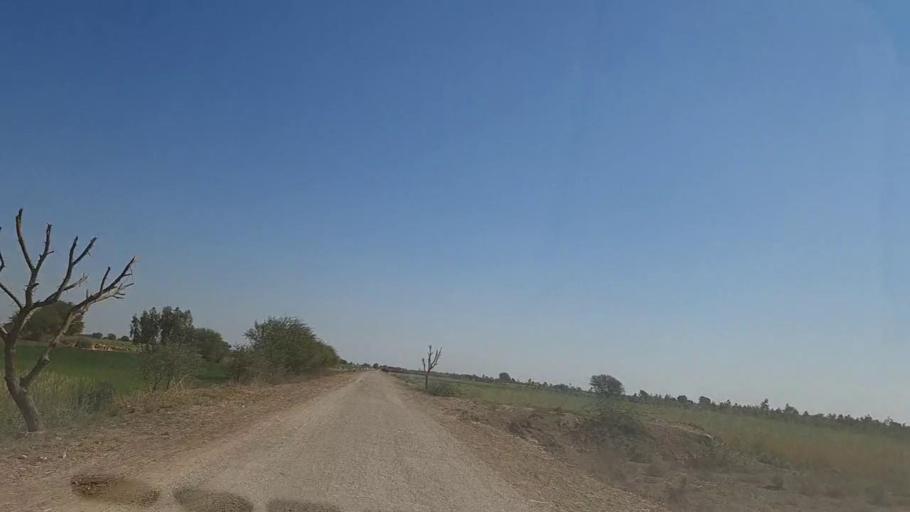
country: PK
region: Sindh
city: Digri
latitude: 25.1106
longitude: 69.1183
